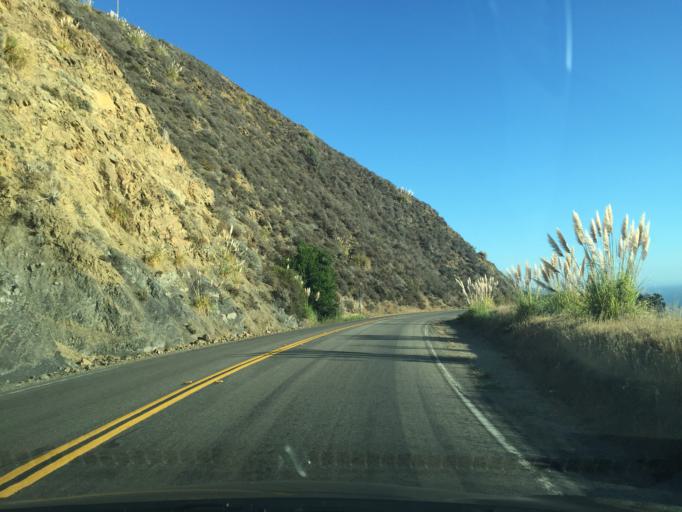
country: US
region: California
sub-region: San Luis Obispo County
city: Cambria
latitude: 35.7855
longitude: -121.3336
